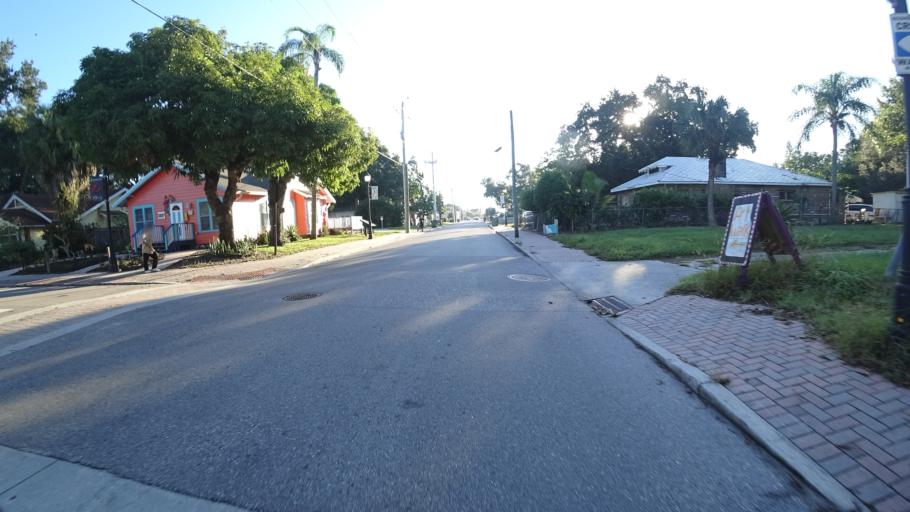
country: US
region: Florida
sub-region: Manatee County
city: Bradenton
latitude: 27.4881
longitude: -82.5733
